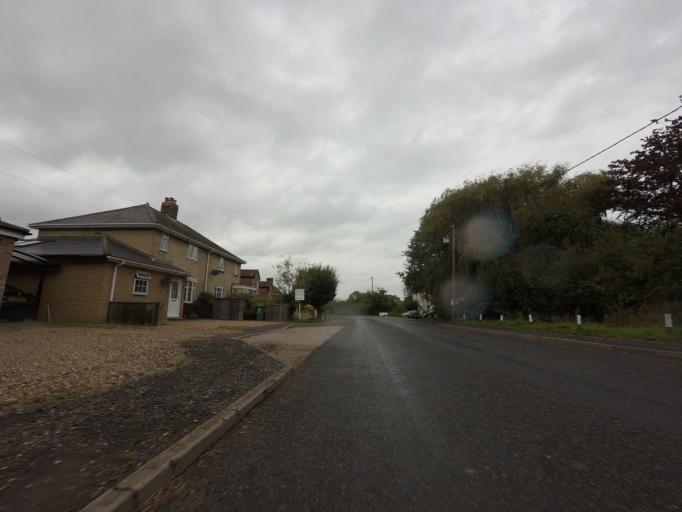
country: GB
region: England
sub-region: Cambridgeshire
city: Comberton
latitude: 52.1584
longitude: 0.0022
